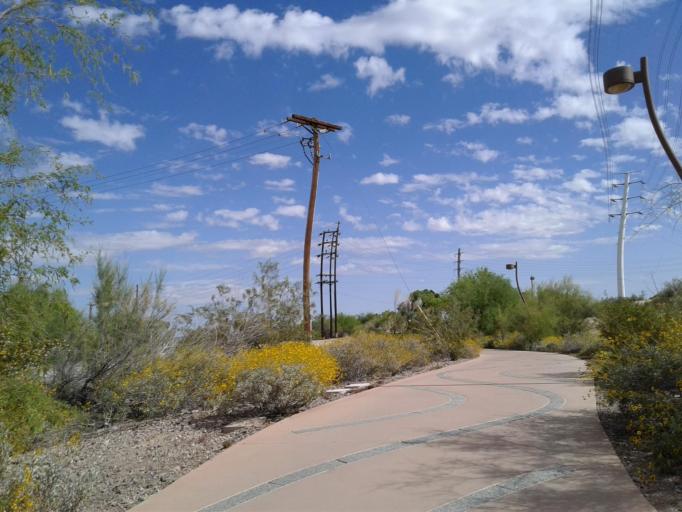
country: US
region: Arizona
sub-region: Maricopa County
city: Tempe Junction
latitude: 33.4515
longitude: -111.9408
